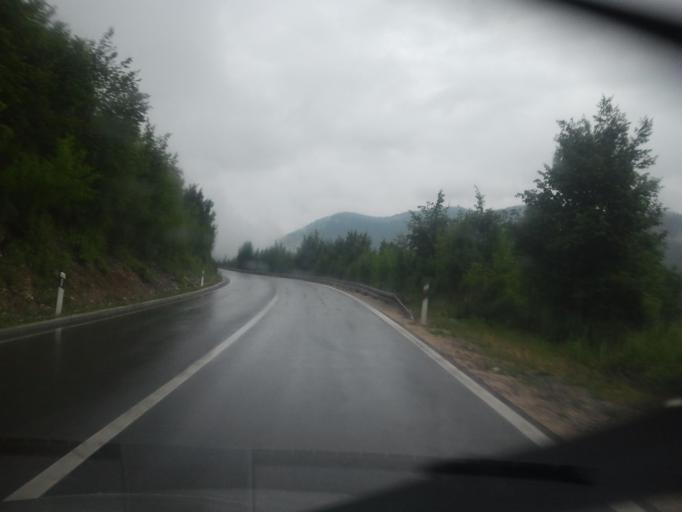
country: HR
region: Zadarska
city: Gracac
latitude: 44.2821
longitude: 15.8229
